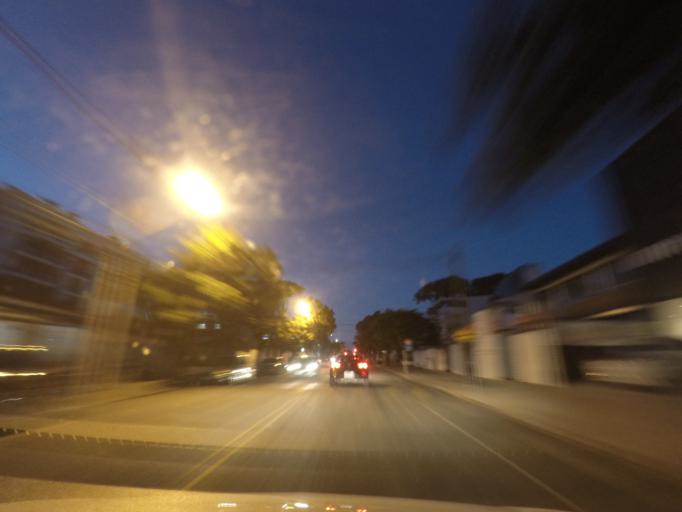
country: BR
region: Parana
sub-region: Curitiba
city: Curitiba
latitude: -25.4557
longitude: -49.2778
